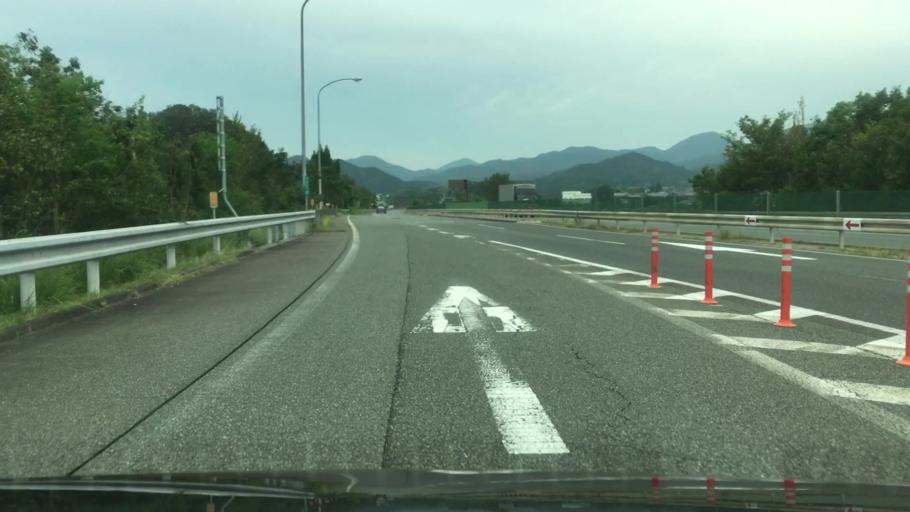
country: JP
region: Hyogo
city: Sasayama
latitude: 35.0676
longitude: 135.1782
